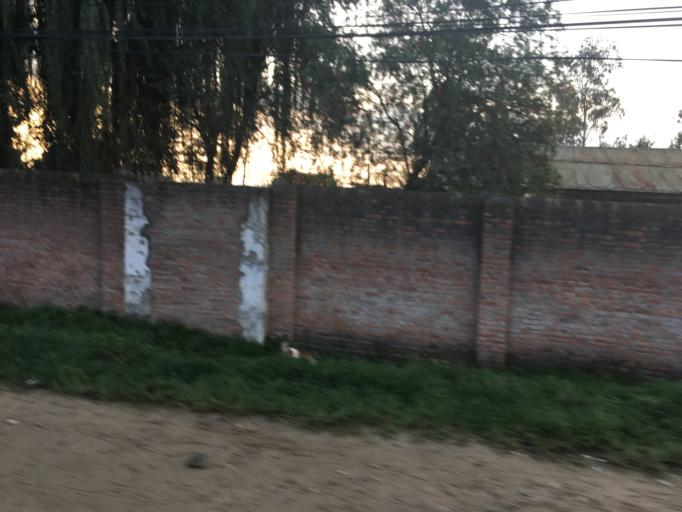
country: NP
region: Central Region
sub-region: Bagmati Zone
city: Bhaktapur
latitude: 27.6829
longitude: 85.4471
